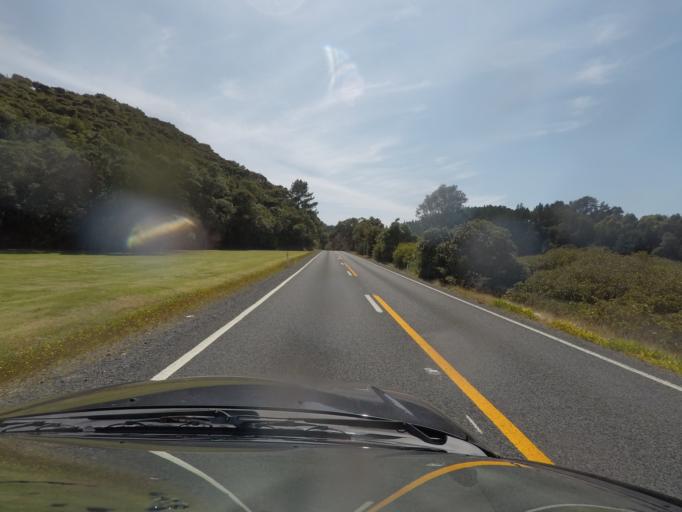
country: NZ
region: Auckland
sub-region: Auckland
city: Warkworth
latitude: -36.3076
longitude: 174.7796
